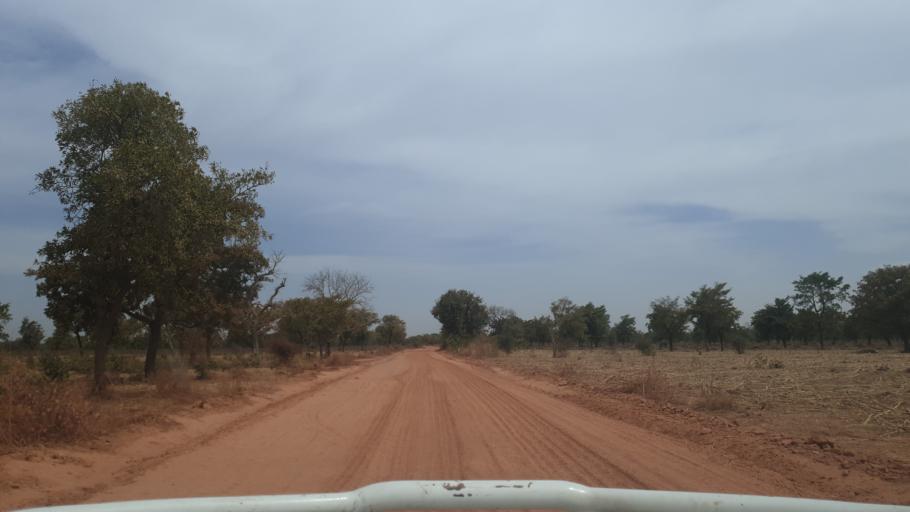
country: ML
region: Sikasso
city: Yorosso
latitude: 12.2202
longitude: -4.7547
